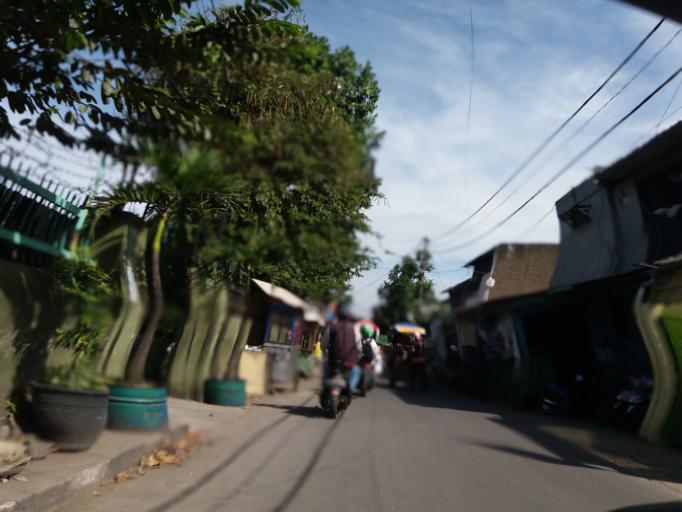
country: ID
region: West Java
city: Bandung
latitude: -6.9440
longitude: 107.6028
